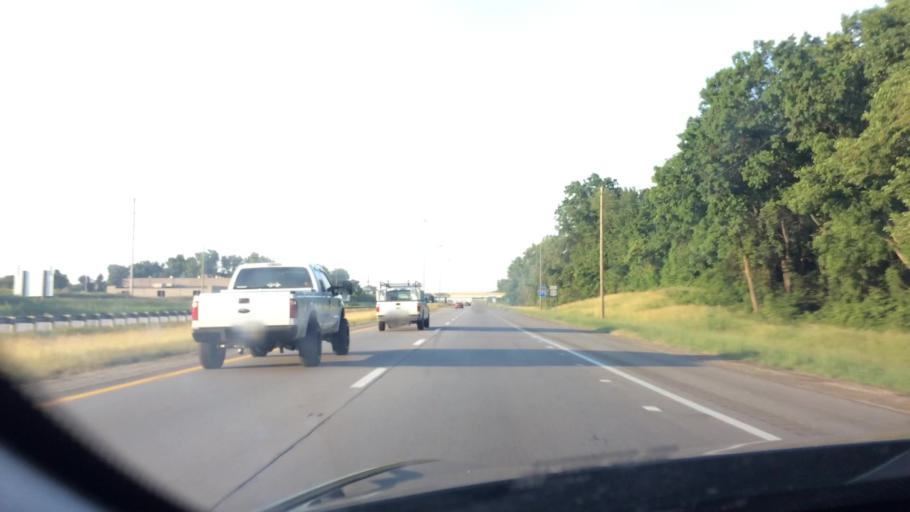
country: US
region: Ohio
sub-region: Lucas County
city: Holland
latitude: 41.6052
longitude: -83.6916
